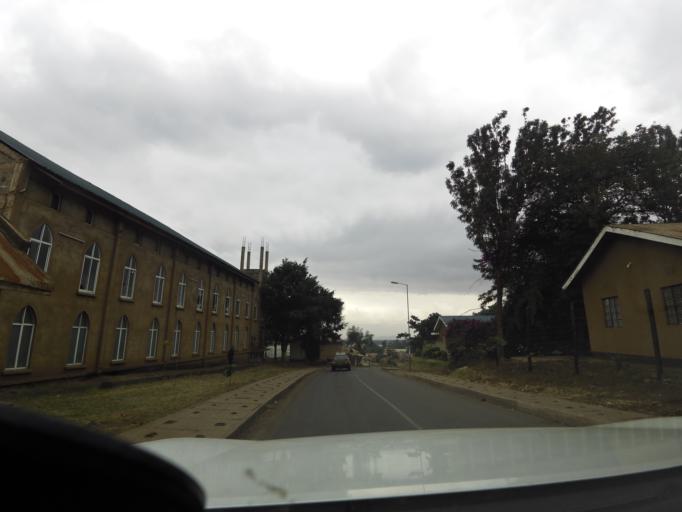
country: TZ
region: Arusha
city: Arusha
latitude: -3.3665
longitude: 36.6611
